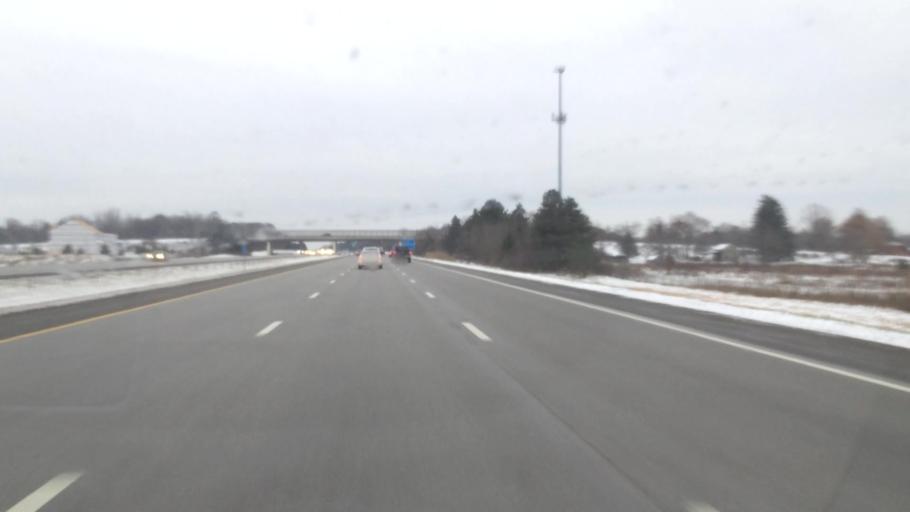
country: US
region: Ohio
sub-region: Medina County
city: Brunswick
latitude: 41.2642
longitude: -81.8049
